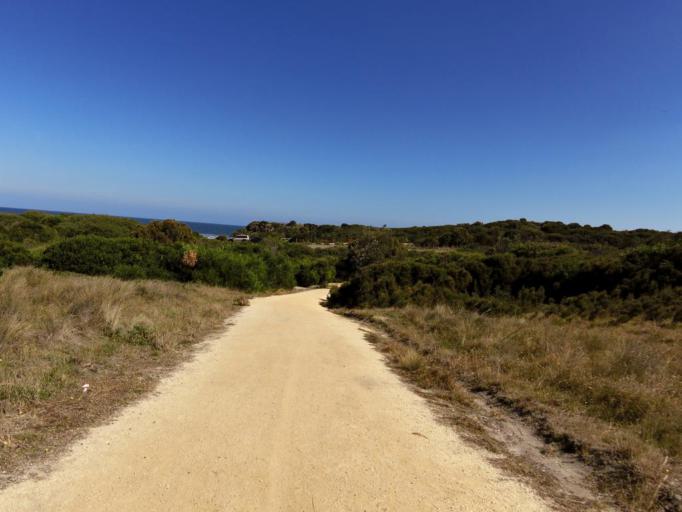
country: AU
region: Victoria
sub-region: Bass Coast
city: North Wonthaggi
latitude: -38.5493
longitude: 145.4719
